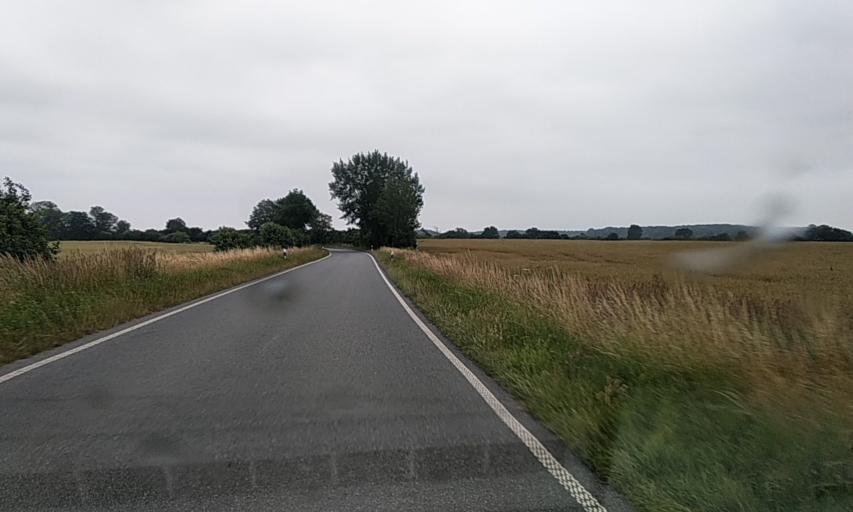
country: DE
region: Schleswig-Holstein
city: Loit
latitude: 54.6070
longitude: 9.7206
